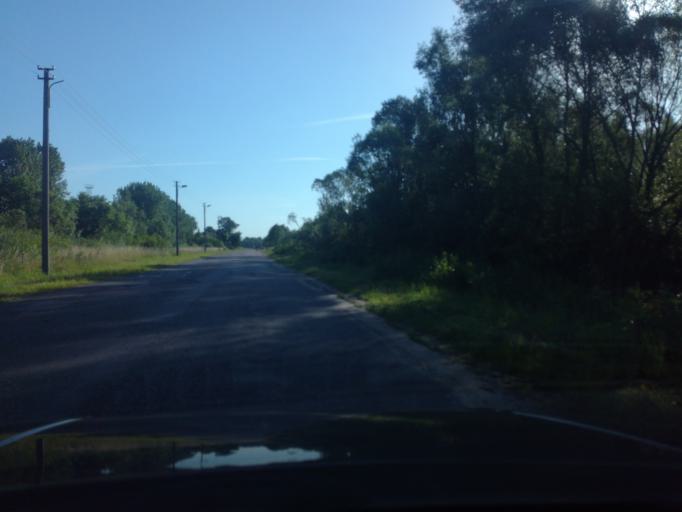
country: LT
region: Alytaus apskritis
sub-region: Alytus
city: Alytus
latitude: 54.4009
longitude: 23.9870
